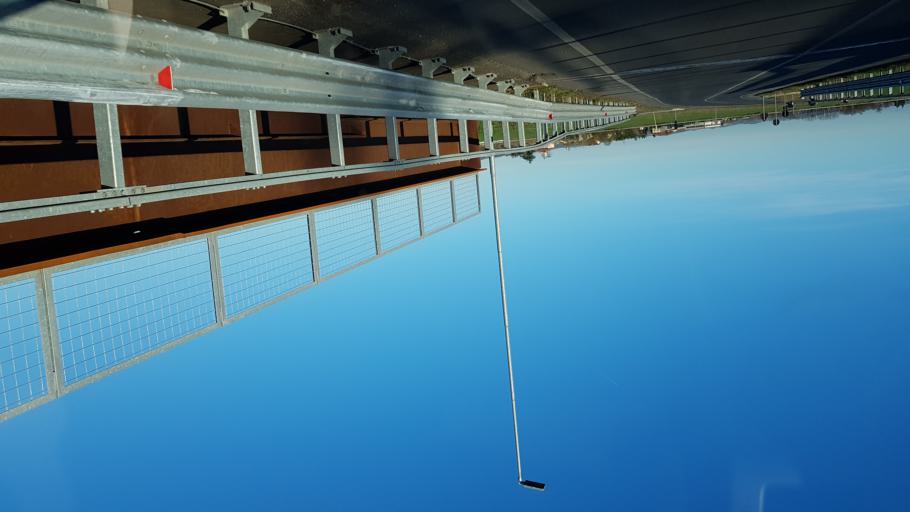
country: IT
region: Piedmont
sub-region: Provincia di Alessandria
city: Serravalle Scrivia
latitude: 44.7387
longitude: 8.8350
